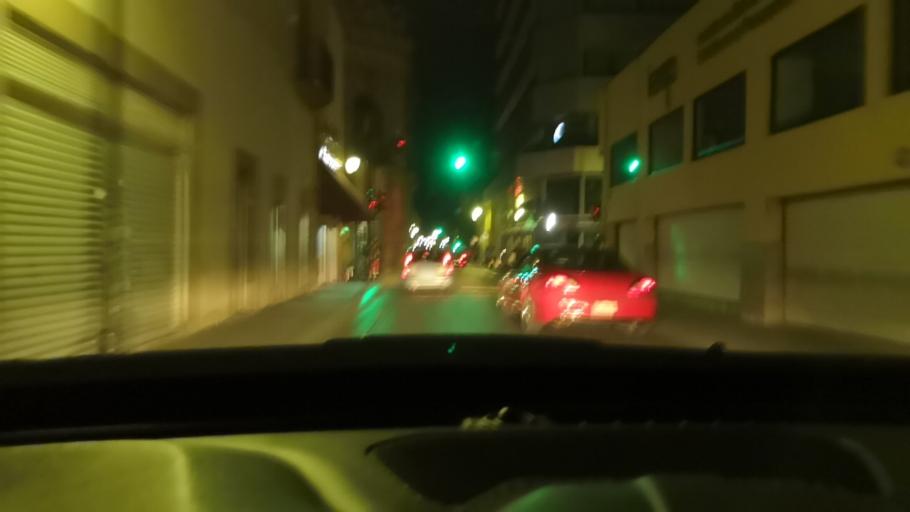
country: MX
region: Guanajuato
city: Leon
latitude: 21.1212
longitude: -101.6827
